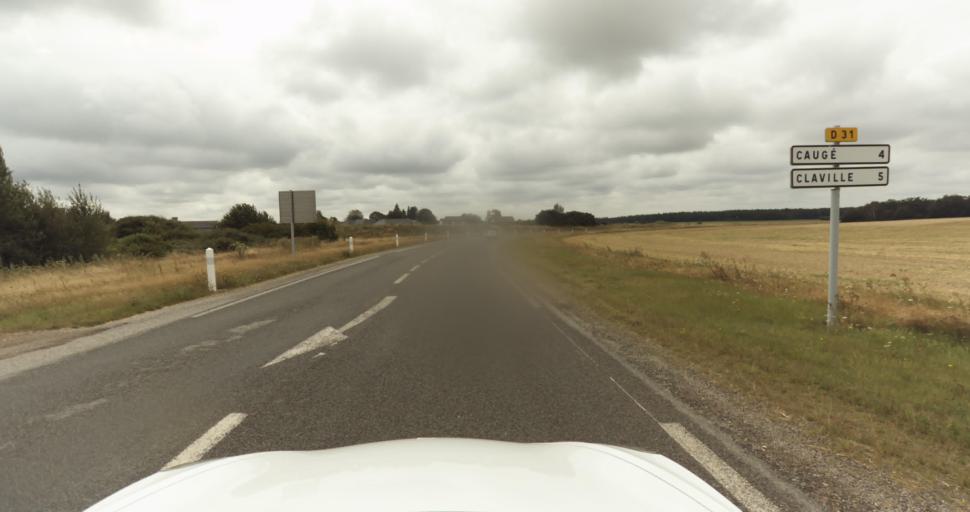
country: FR
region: Haute-Normandie
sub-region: Departement de l'Eure
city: Saint-Sebastien-de-Morsent
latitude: 49.0356
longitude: 1.0892
